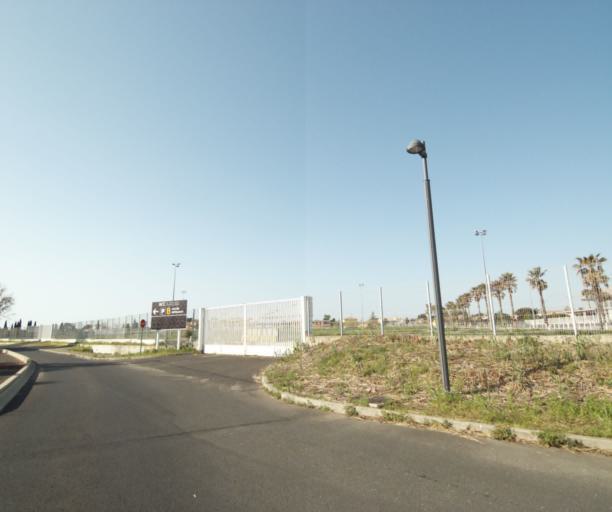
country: FR
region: Languedoc-Roussillon
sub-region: Departement de l'Herault
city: Perols
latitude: 43.5708
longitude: 3.9548
